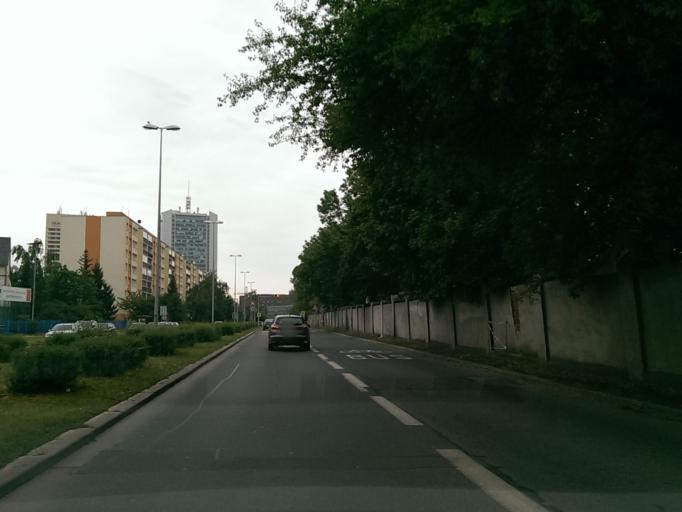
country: CZ
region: Praha
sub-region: Praha 4
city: Hodkovicky
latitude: 50.0450
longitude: 14.4393
